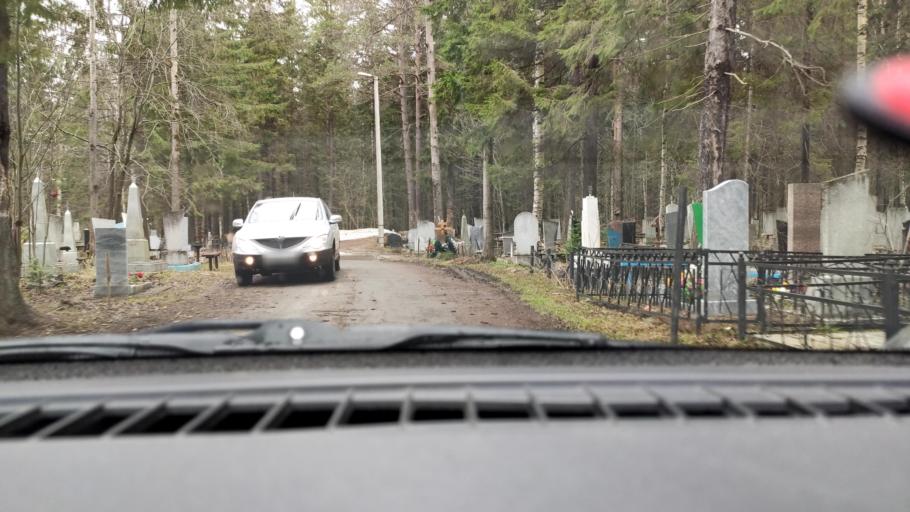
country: RU
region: Perm
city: Polazna
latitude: 58.1393
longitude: 56.4146
